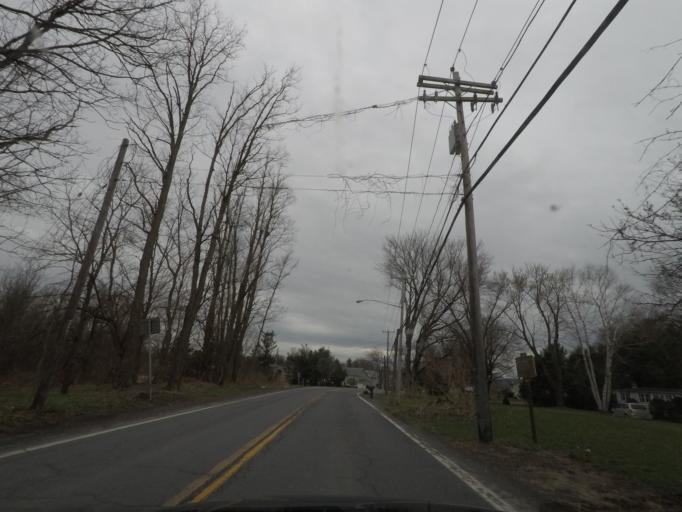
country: US
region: New York
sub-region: Rensselaer County
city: Castleton-on-Hudson
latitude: 42.5467
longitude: -73.8128
